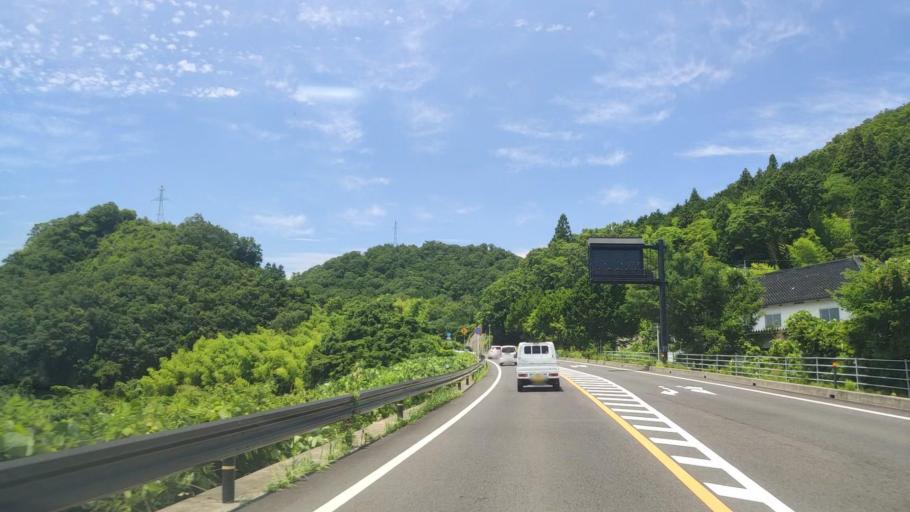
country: JP
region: Tottori
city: Tottori
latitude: 35.3987
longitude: 134.2681
